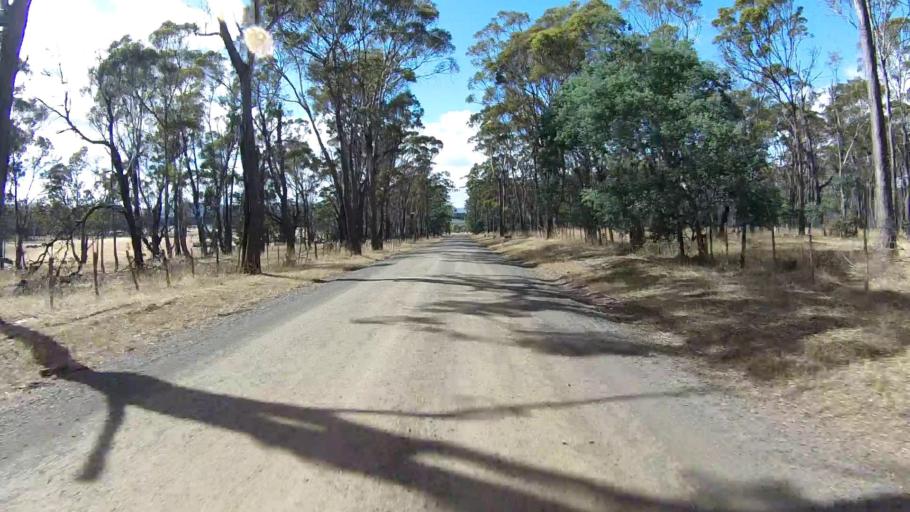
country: AU
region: Tasmania
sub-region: Northern Midlands
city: Evandale
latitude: -41.7295
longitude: 147.4446
